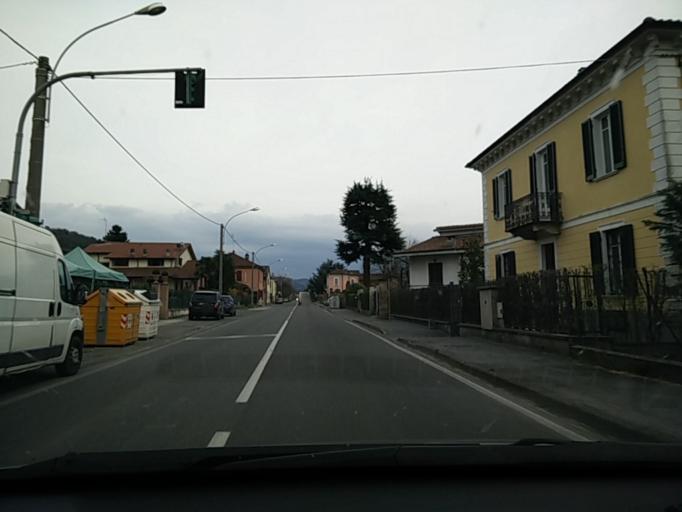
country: IT
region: Lombardy
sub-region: Provincia di Pavia
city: Rivanazzano
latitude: 44.9279
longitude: 9.0227
